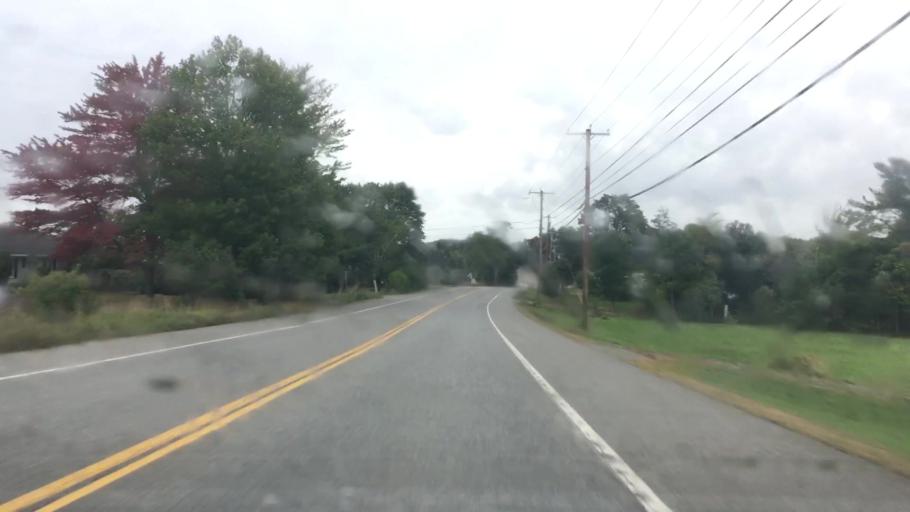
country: US
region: Maine
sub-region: Penobscot County
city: Orrington
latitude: 44.7206
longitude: -68.8262
